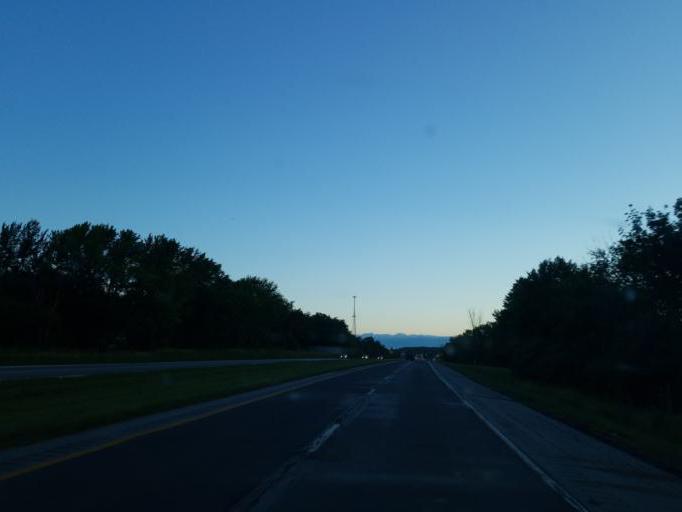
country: US
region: Ohio
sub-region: Wayne County
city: Doylestown
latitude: 40.9839
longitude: -81.6633
